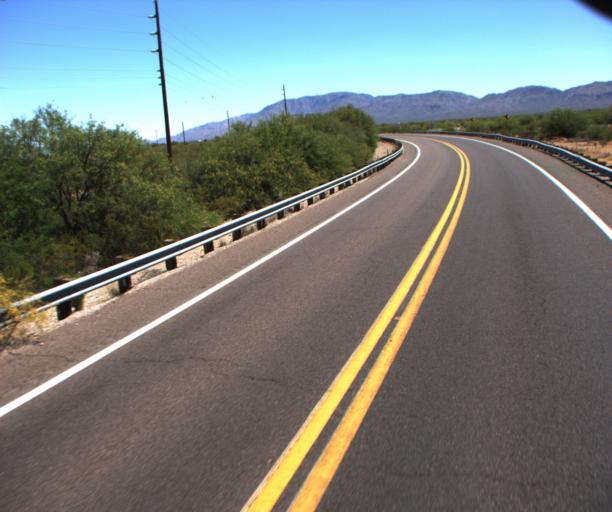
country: US
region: Arizona
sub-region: La Paz County
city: Salome
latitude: 33.8234
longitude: -113.5312
